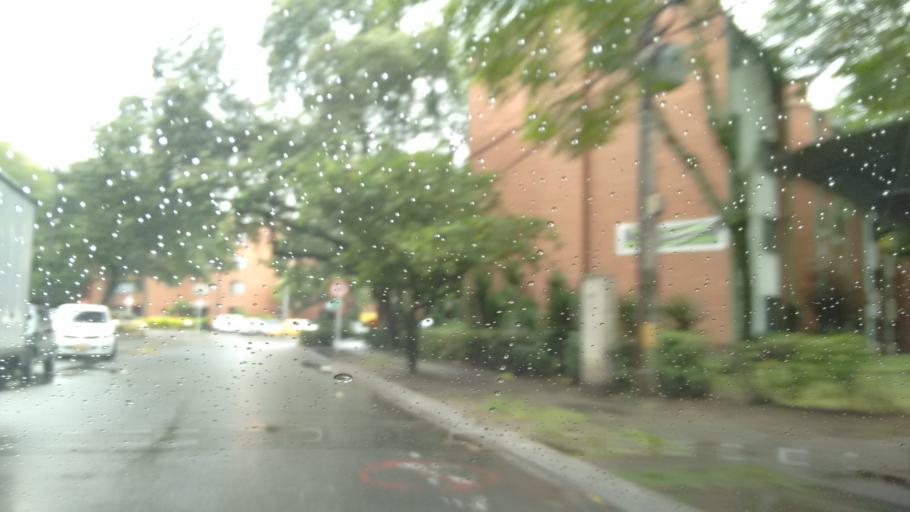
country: CO
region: Antioquia
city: Medellin
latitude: 6.2569
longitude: -75.5778
